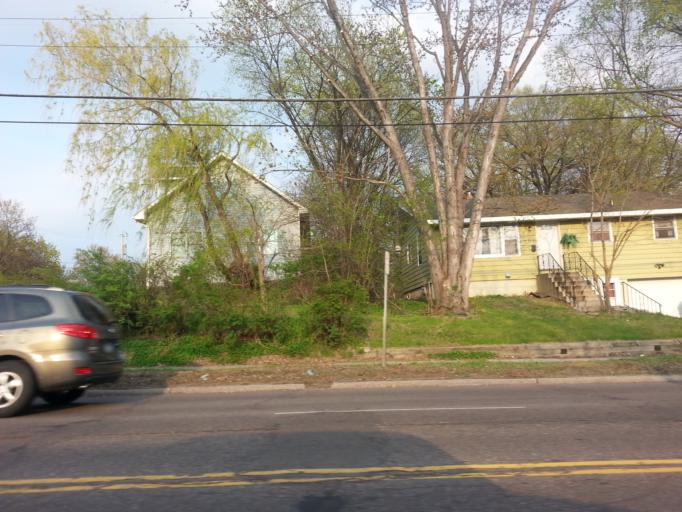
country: US
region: Minnesota
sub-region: Ramsey County
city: Maplewood
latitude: 44.9539
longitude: -93.0253
